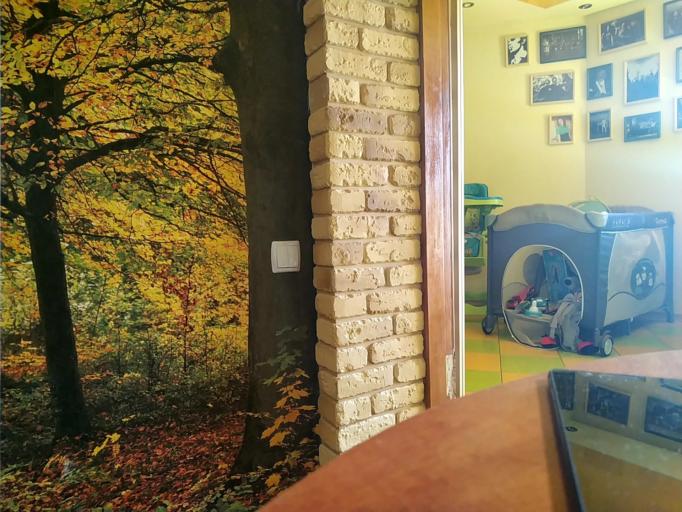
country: RU
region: Tverskaya
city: Vydropuzhsk
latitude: 57.4368
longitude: 34.7480
